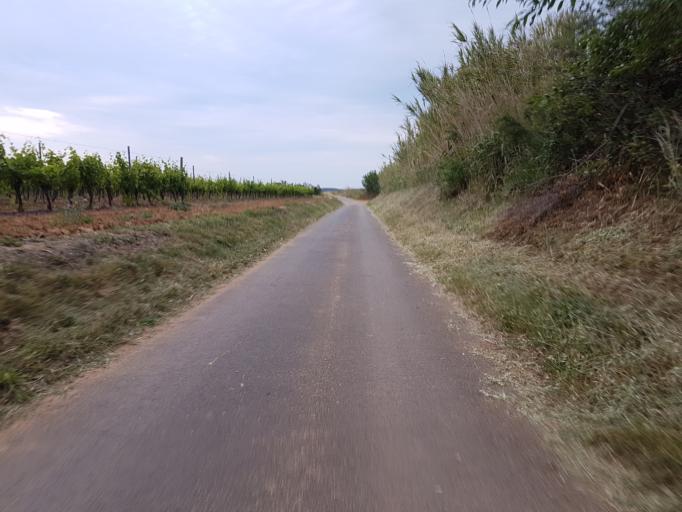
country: FR
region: Languedoc-Roussillon
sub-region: Departement de l'Herault
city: Cers
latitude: 43.3184
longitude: 3.3215
